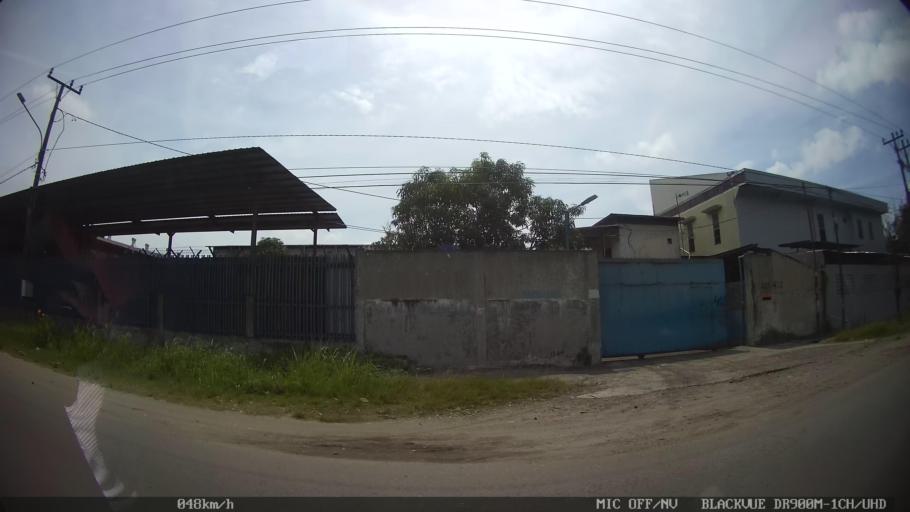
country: ID
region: North Sumatra
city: Medan
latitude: 3.6403
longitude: 98.7165
